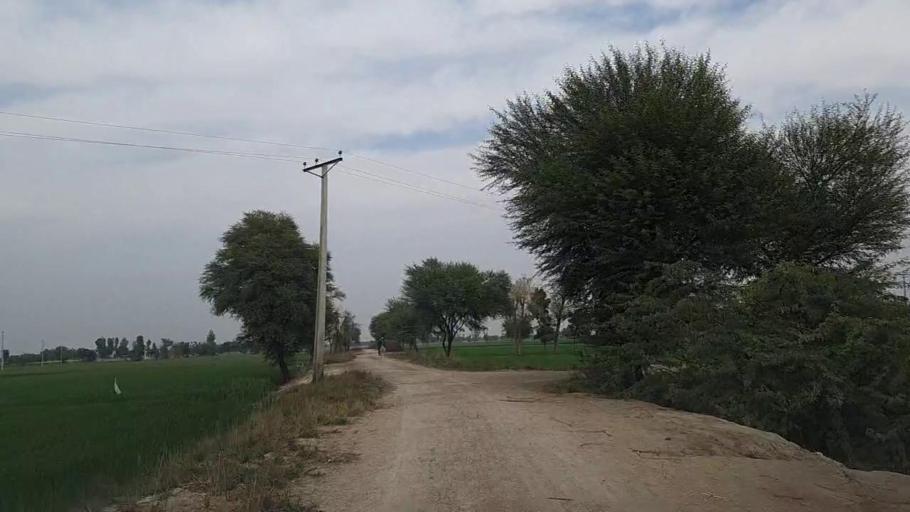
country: PK
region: Sindh
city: Daur
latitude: 26.4382
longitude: 68.4708
